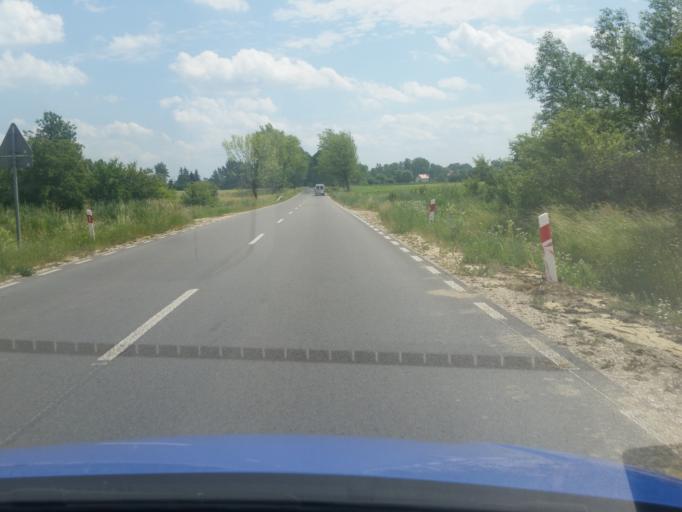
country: PL
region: Swietokrzyskie
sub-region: Powiat kazimierski
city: Kazimierza Wielka
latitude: 50.2951
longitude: 20.5200
